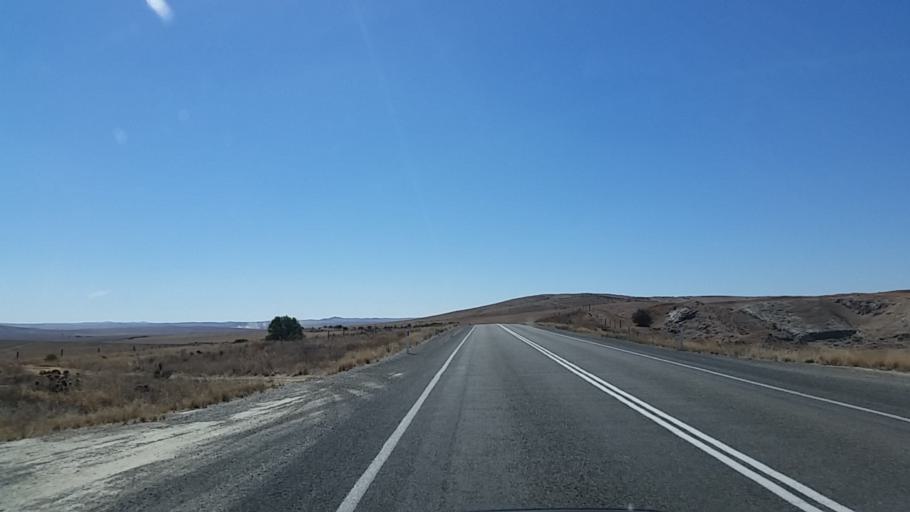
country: AU
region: South Australia
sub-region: Northern Areas
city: Jamestown
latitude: -33.3318
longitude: 138.8897
